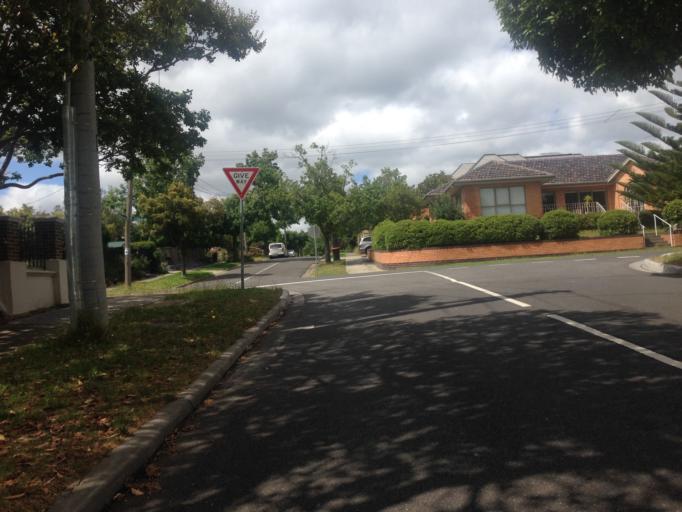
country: AU
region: Victoria
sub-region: Boroondara
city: Balwyn North
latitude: -37.7847
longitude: 145.0821
